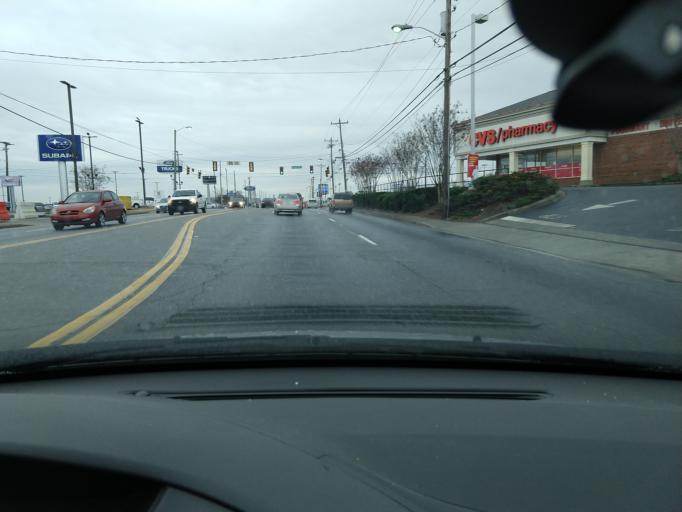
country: US
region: South Carolina
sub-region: Greenville County
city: Greenville
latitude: 34.8353
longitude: -82.3530
